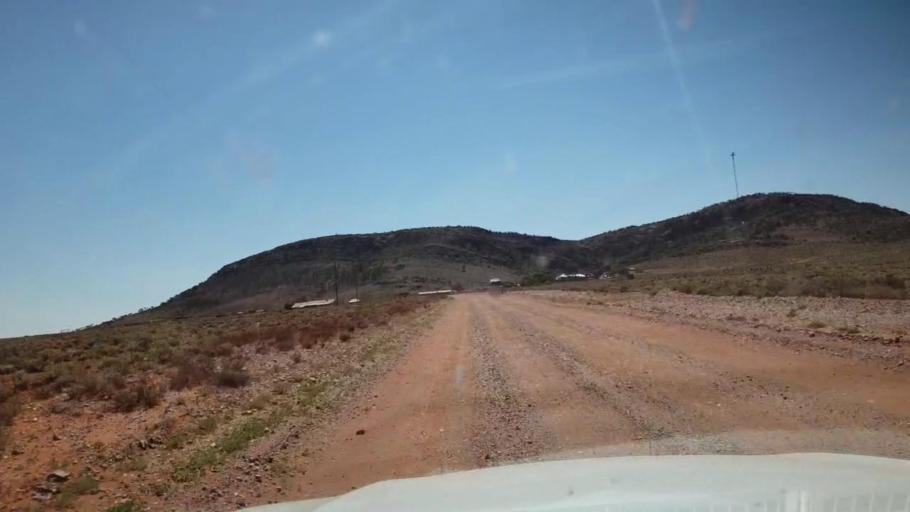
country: AU
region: South Australia
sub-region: Whyalla
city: Whyalla
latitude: -32.6892
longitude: 137.1276
